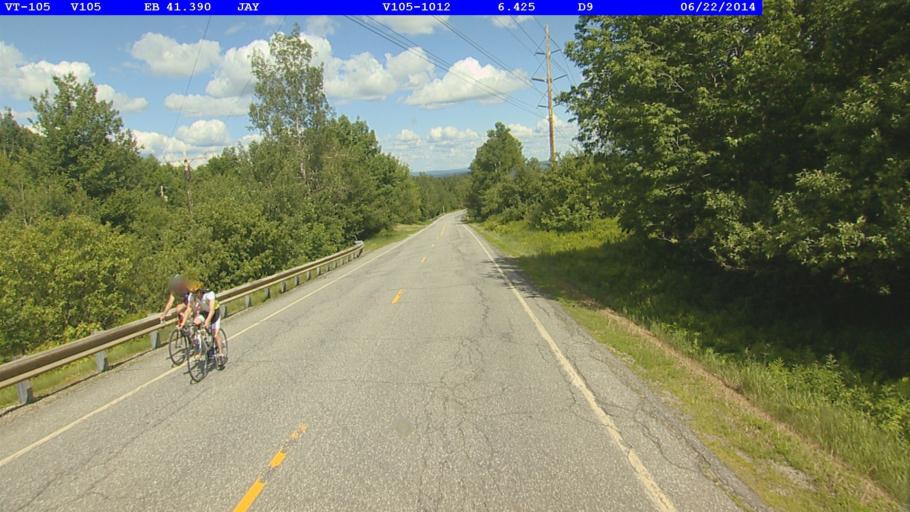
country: CA
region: Quebec
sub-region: Monteregie
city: Sutton
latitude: 44.9727
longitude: -72.4591
